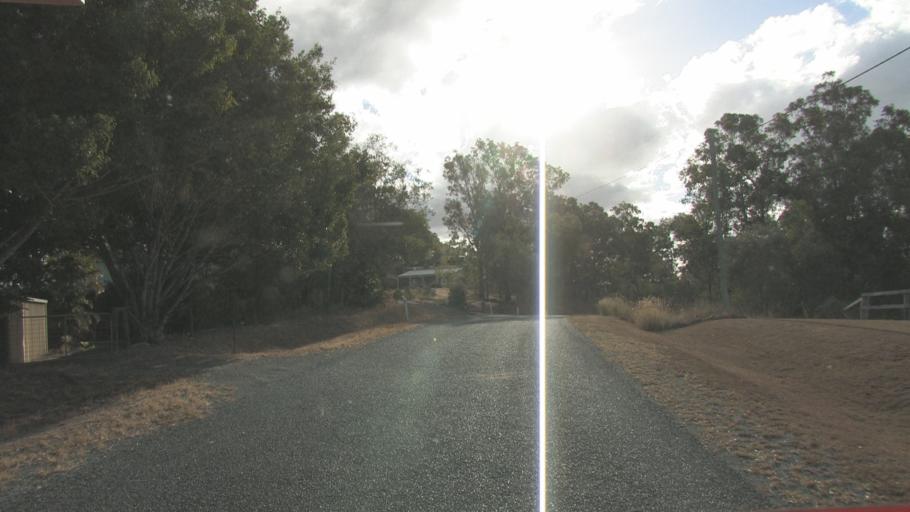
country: AU
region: Queensland
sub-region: Logan
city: Cedar Vale
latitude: -27.8998
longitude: 153.0724
